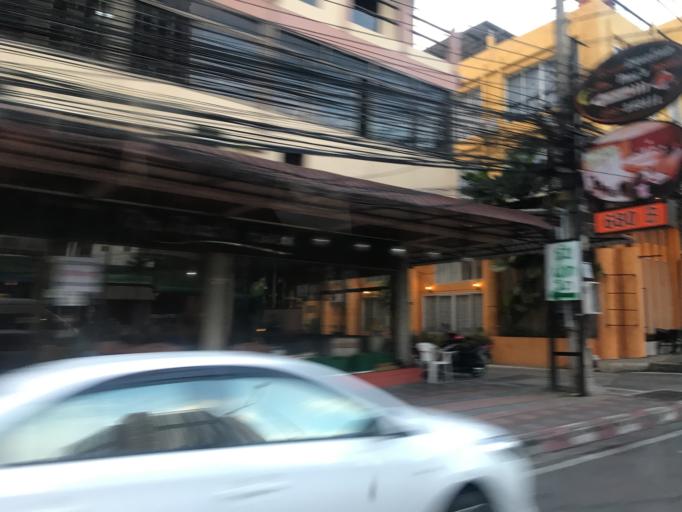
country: TH
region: Chon Buri
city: Phatthaya
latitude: 12.9192
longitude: 100.8718
